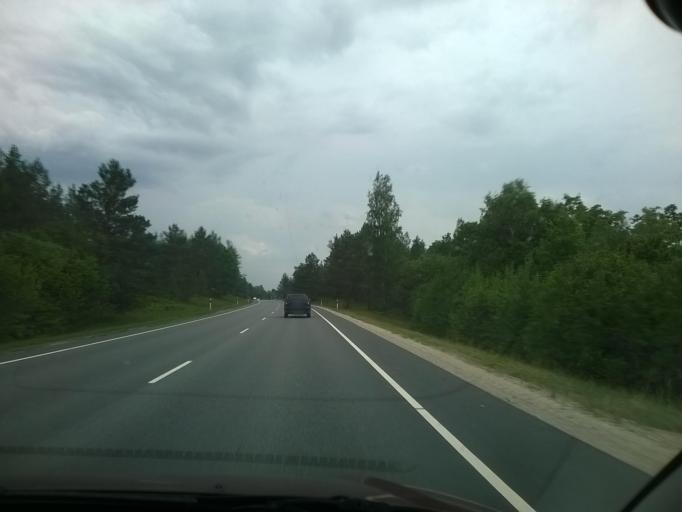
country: EE
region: Harju
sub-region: Nissi vald
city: Turba
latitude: 59.1049
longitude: 24.2532
